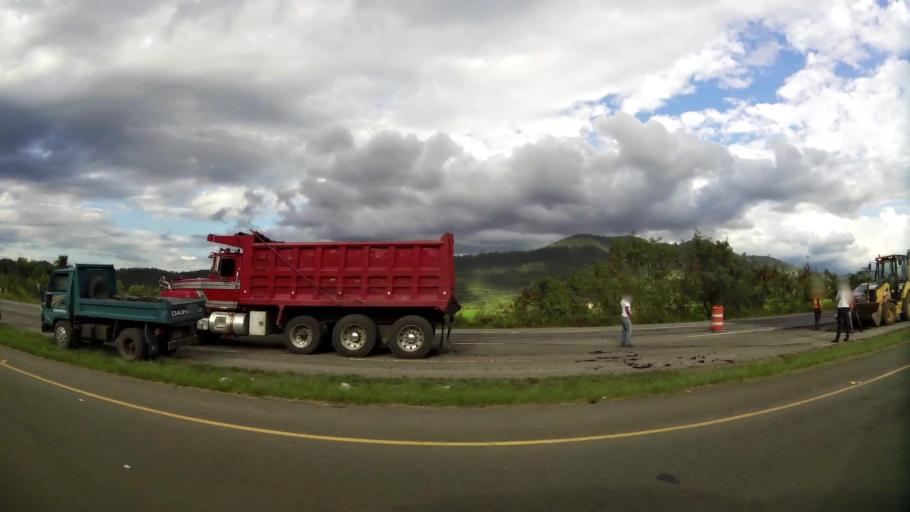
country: DO
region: Monsenor Nouel
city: Bonao
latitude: 18.9001
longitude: -70.3705
